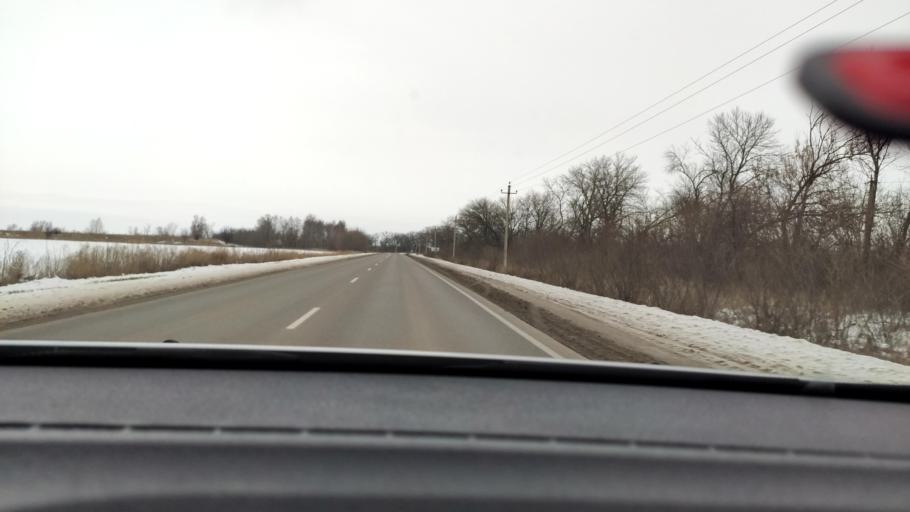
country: RU
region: Voronezj
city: Semiluki
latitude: 51.7257
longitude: 38.9899
